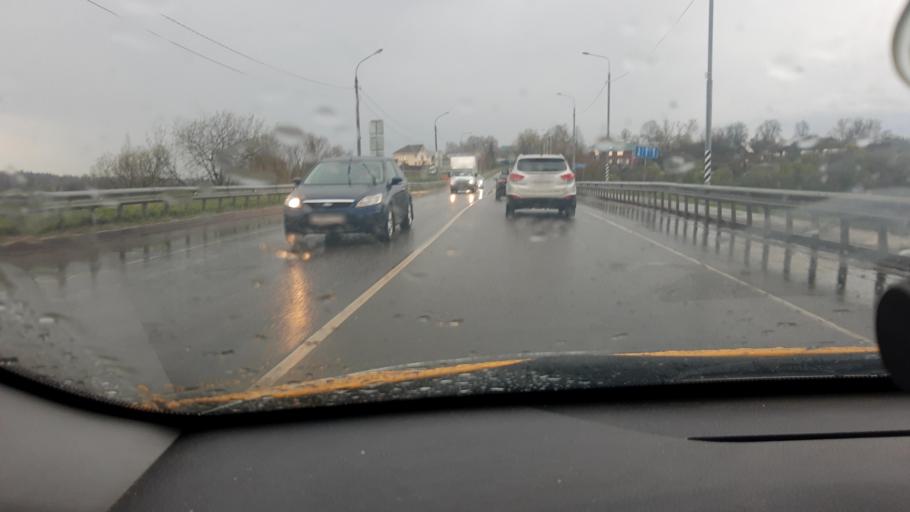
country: RU
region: Moskovskaya
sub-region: Volokolamskiy Rayon
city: Volokolamsk
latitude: 56.0080
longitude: 35.9276
